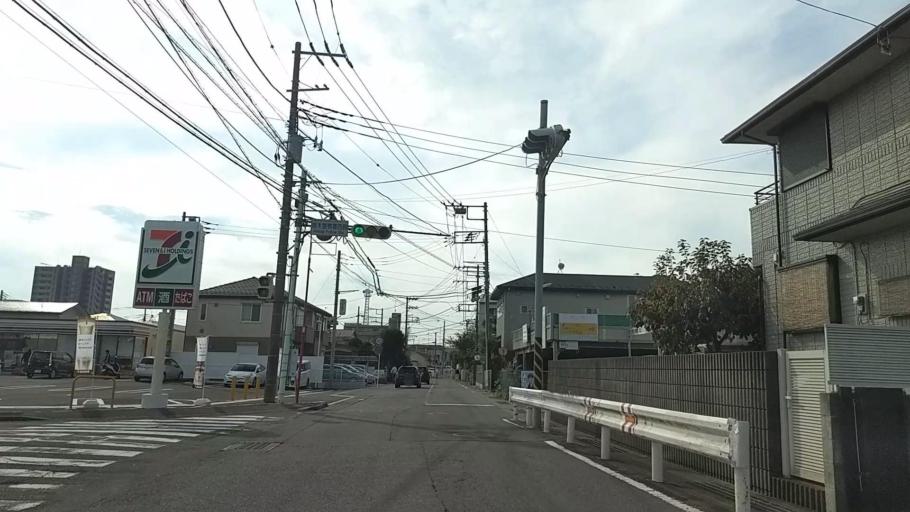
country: JP
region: Kanagawa
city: Atsugi
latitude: 35.4464
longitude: 139.3544
